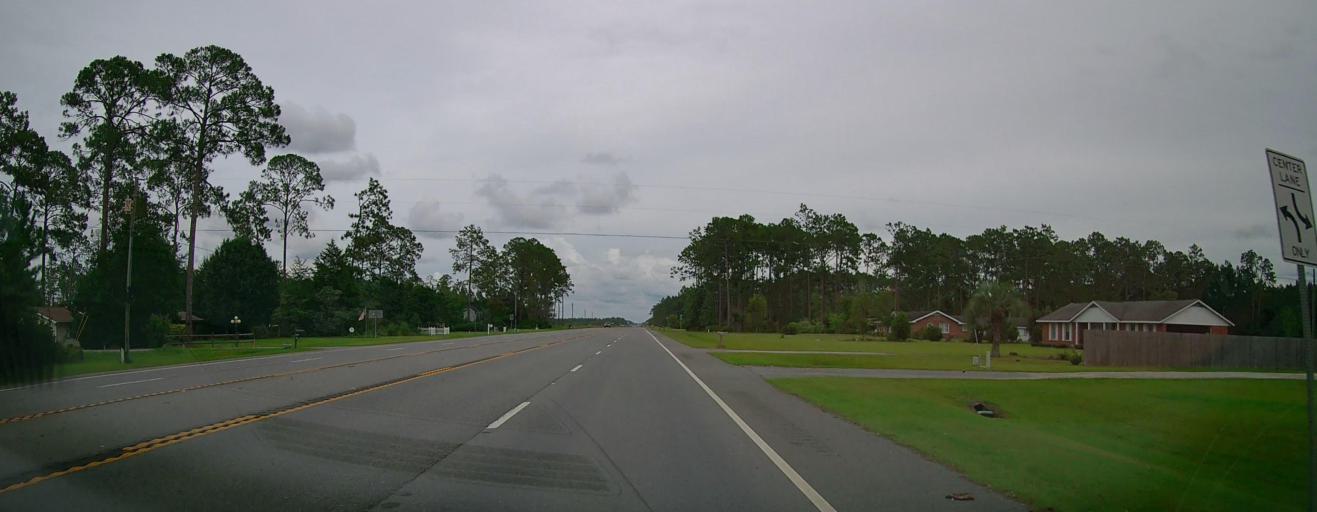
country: US
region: Georgia
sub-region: Appling County
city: Baxley
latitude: 31.7620
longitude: -82.3012
